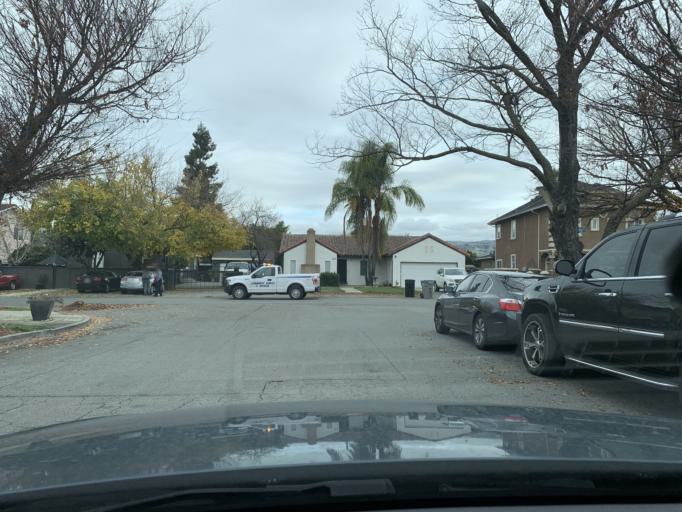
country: US
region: California
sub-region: Santa Clara County
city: Alum Rock
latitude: 37.3476
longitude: -121.8380
